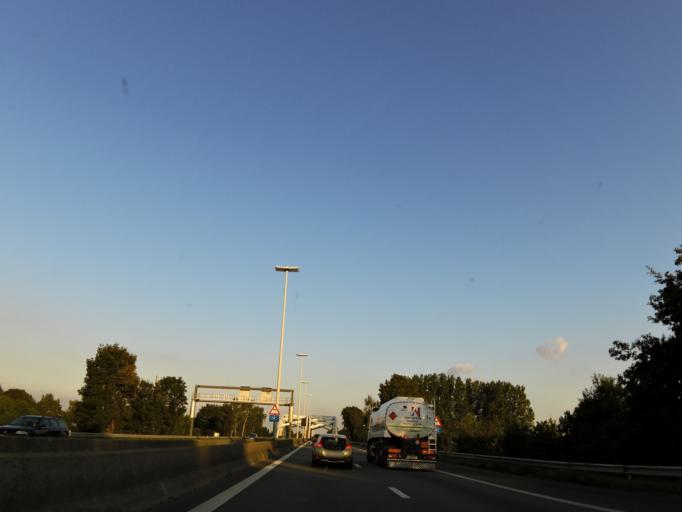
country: BE
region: Flanders
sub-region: Provincie Antwerpen
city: Zandhoven
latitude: 51.1880
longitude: 4.6631
